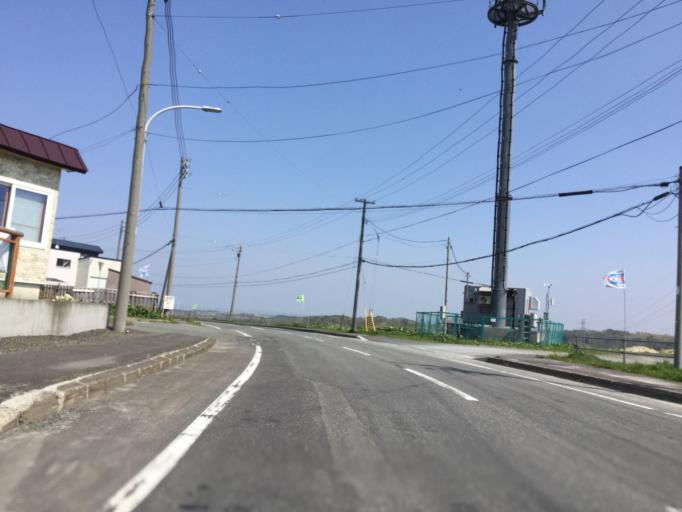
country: JP
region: Hokkaido
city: Wakkanai
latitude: 45.3809
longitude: 141.6751
